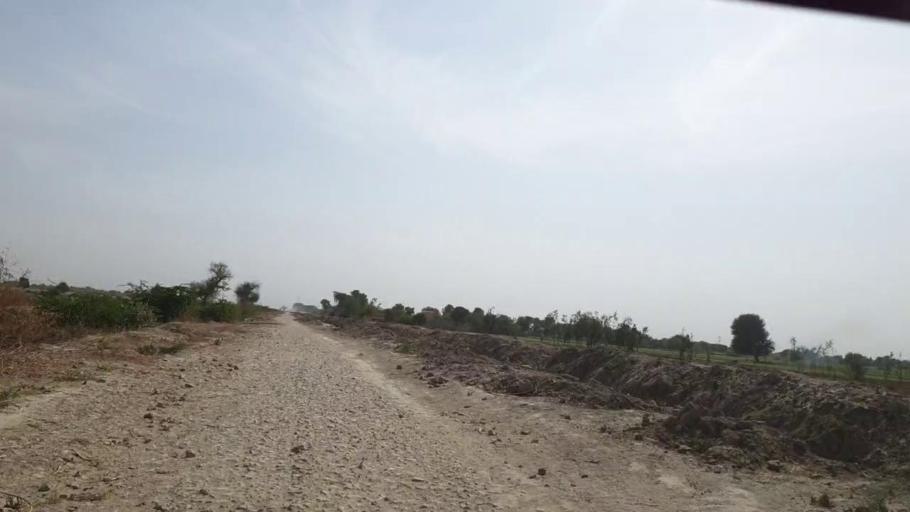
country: PK
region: Sindh
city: Nabisar
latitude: 25.0646
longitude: 69.5780
